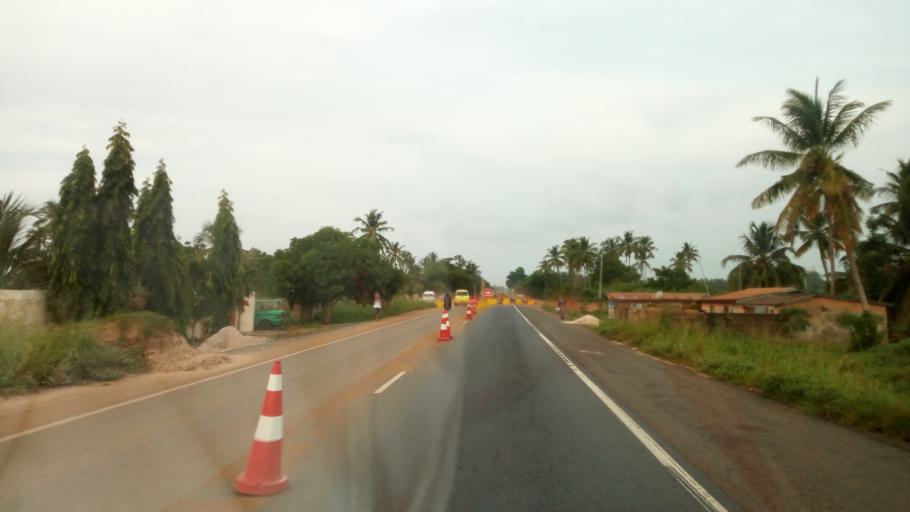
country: TG
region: Maritime
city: Lome
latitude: 6.0897
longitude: 1.0677
